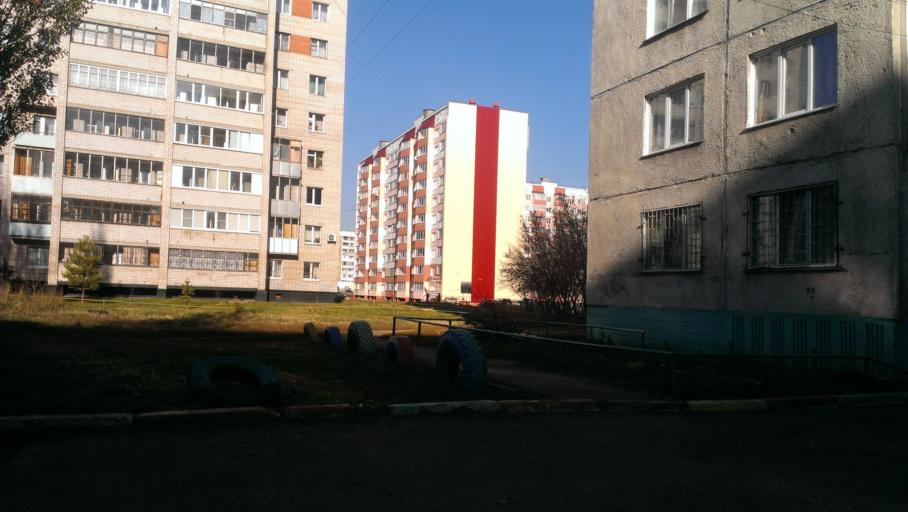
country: RU
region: Altai Krai
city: Novosilikatnyy
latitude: 53.3346
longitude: 83.6695
